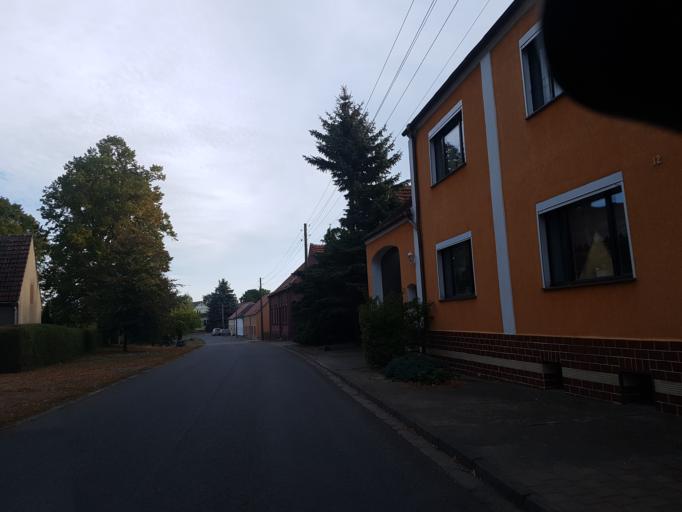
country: DE
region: Brandenburg
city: Dahme
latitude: 51.8616
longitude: 13.3822
